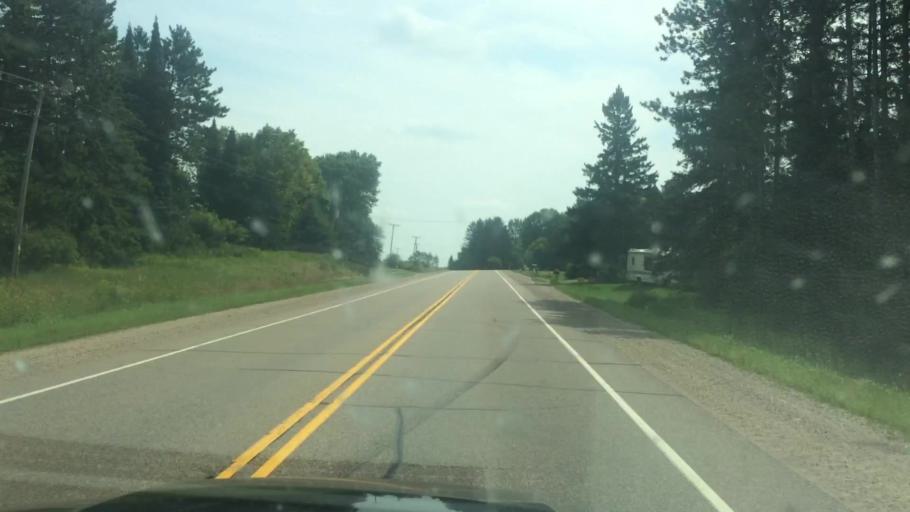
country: US
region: Wisconsin
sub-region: Langlade County
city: Antigo
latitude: 45.1693
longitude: -88.9809
